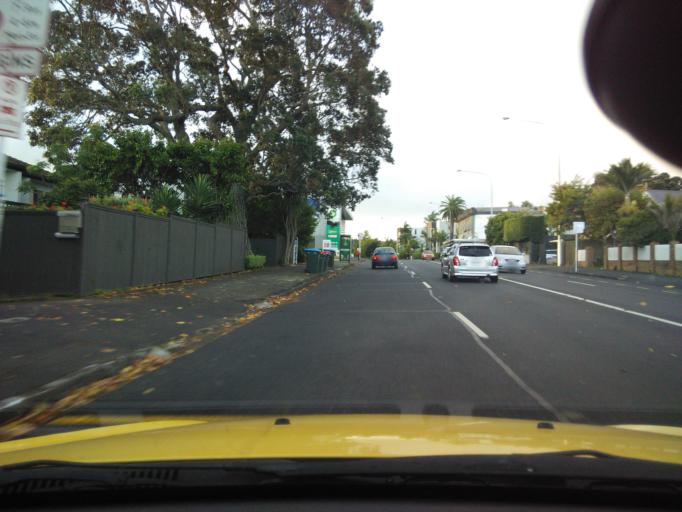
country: NZ
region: Auckland
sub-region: Auckland
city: Auckland
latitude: -36.8980
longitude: 174.7734
